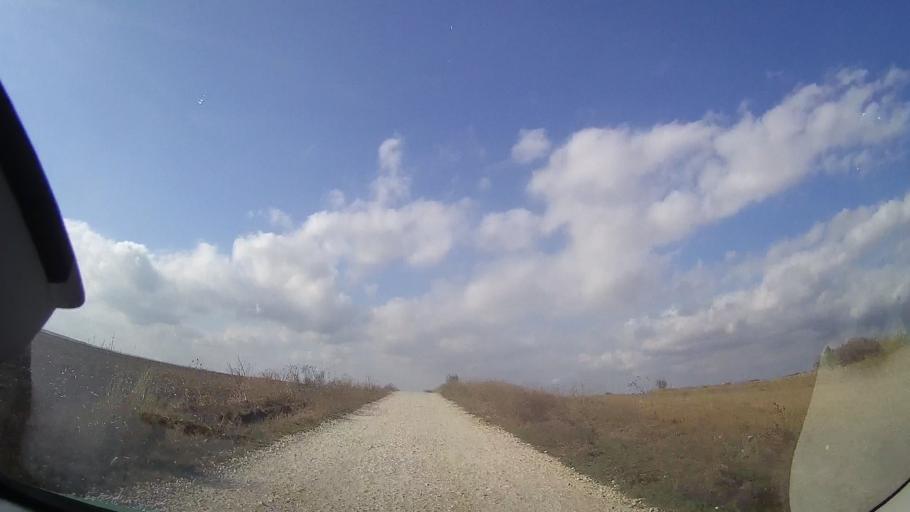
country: RO
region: Constanta
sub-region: Comuna Douazeci si Trei August
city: Douazeci si Trei August
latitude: 43.9110
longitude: 28.5969
